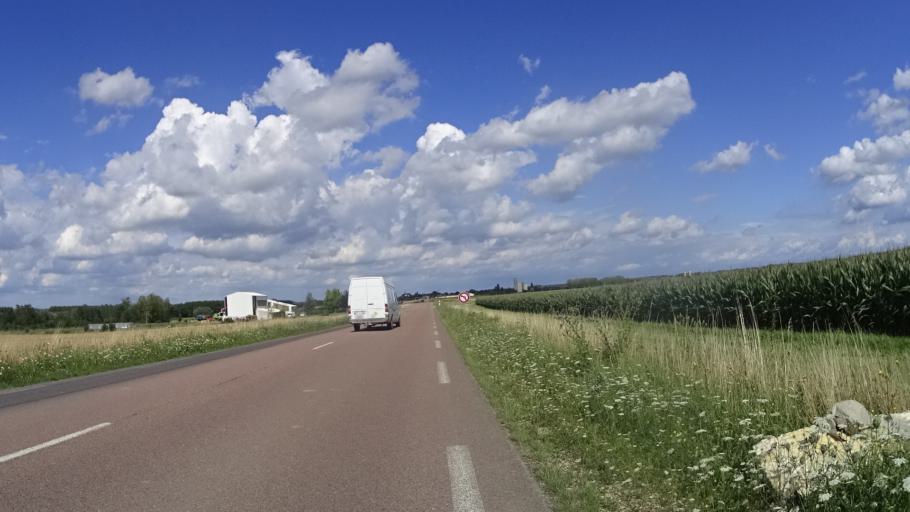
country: FR
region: Champagne-Ardenne
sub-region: Departement de la Marne
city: Pargny-sur-Saulx
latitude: 48.7640
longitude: 4.8138
